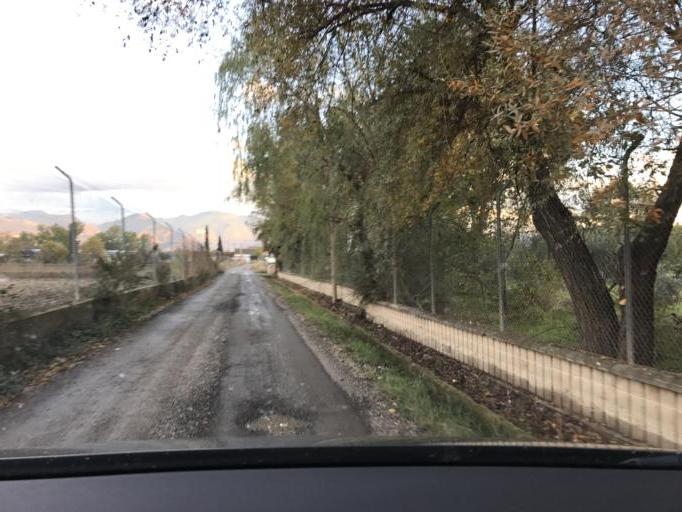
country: ES
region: Andalusia
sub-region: Provincia de Granada
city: Armilla
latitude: 37.1663
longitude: -3.6236
